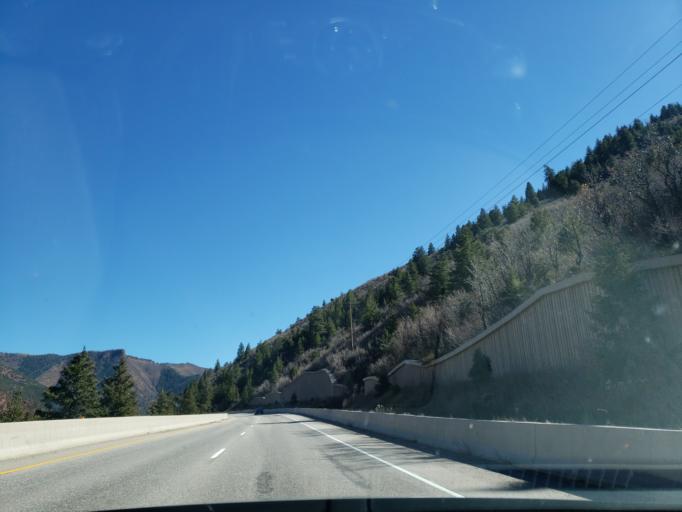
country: US
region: Colorado
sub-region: Eagle County
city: Basalt
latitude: 39.3292
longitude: -106.9724
